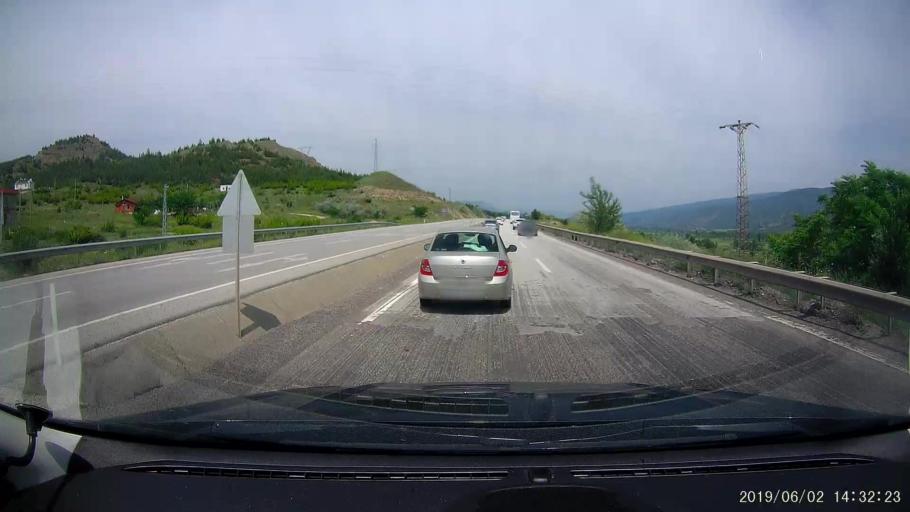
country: TR
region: Kastamonu
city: Tosya
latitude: 41.0249
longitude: 34.1501
